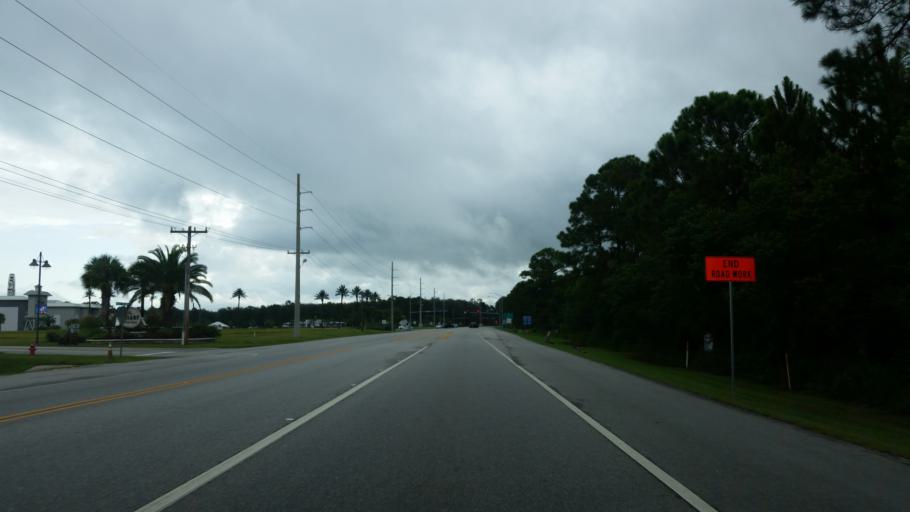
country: US
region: Alabama
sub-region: Baldwin County
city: Orange Beach
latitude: 30.2894
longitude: -87.6323
